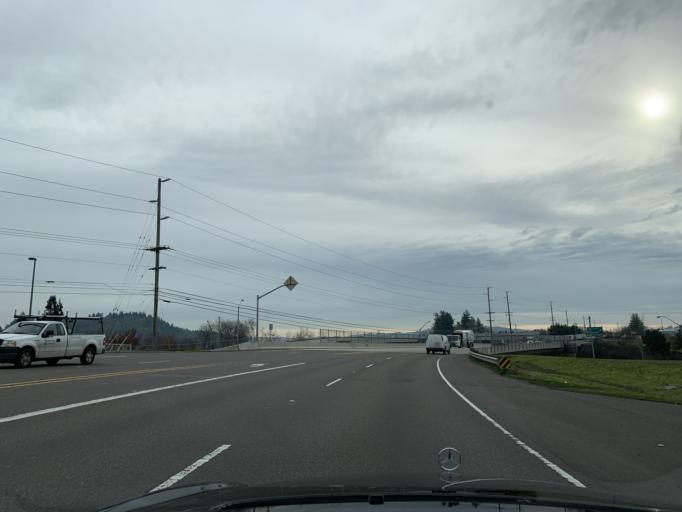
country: US
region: Oregon
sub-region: Clackamas County
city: Clackamas
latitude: 45.4212
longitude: -122.5738
